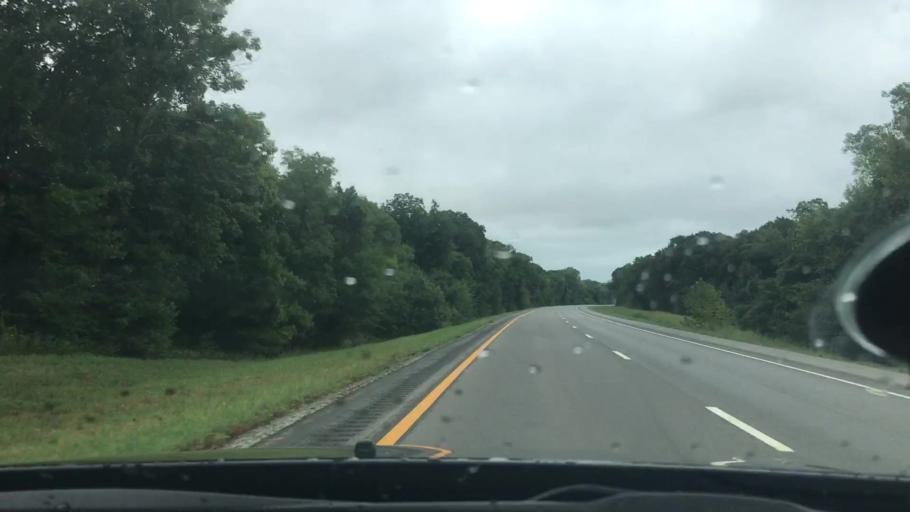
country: US
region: Oklahoma
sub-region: Okmulgee County
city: Morris
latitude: 35.4488
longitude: -95.7573
